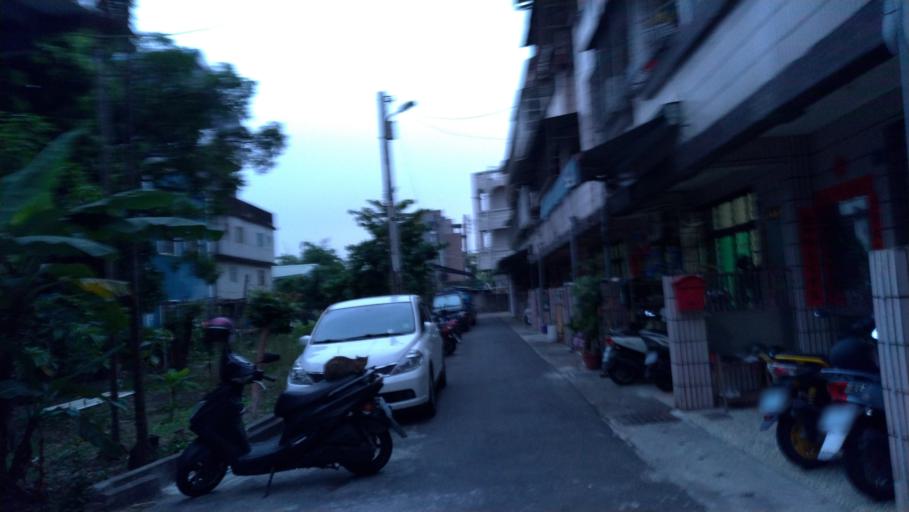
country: TW
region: Taiwan
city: Fengshan
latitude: 22.6529
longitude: 120.3636
